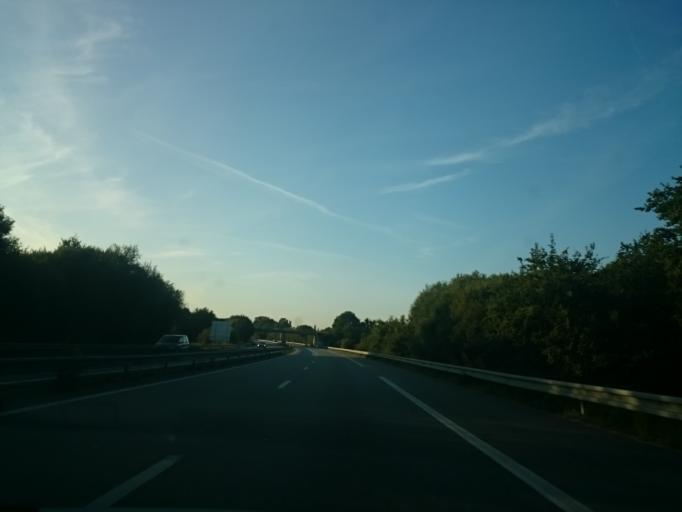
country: FR
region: Brittany
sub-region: Departement du Morbihan
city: Auray
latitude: 47.6781
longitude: -3.0182
